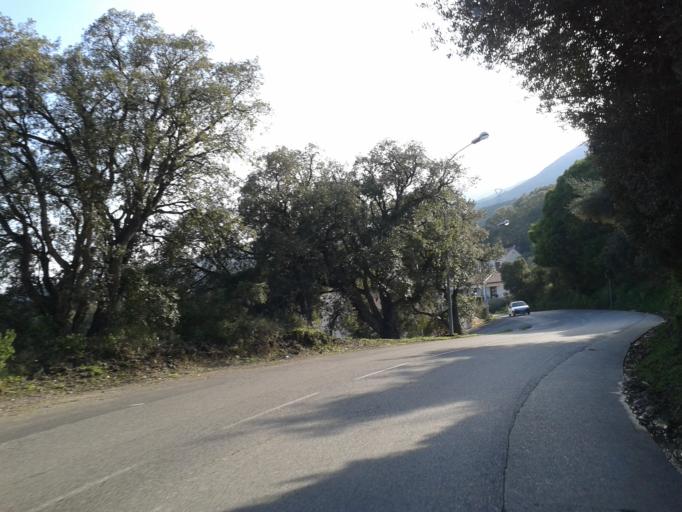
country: FR
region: Corsica
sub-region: Departement de la Haute-Corse
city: Biguglia
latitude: 42.5926
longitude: 9.4282
